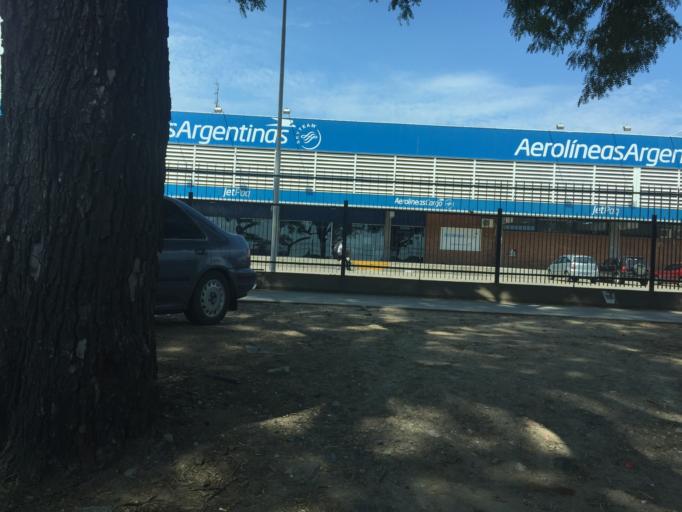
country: AR
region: Buenos Aires F.D.
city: Colegiales
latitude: -34.5542
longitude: -58.4196
